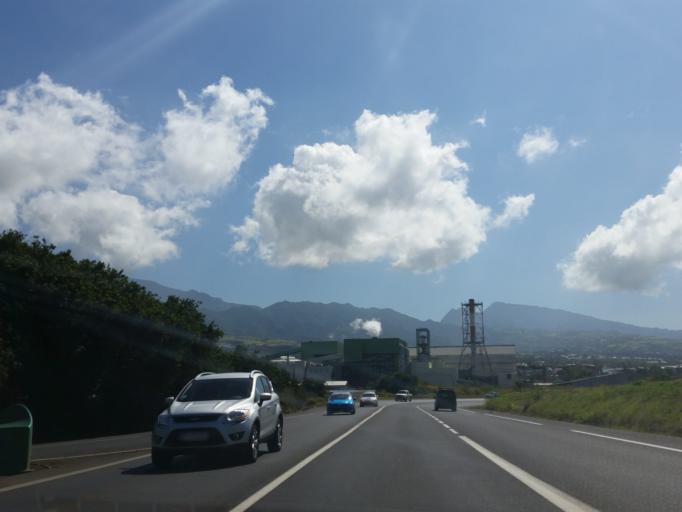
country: RE
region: Reunion
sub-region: Reunion
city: Saint-Louis
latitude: -21.2840
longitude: 55.3953
